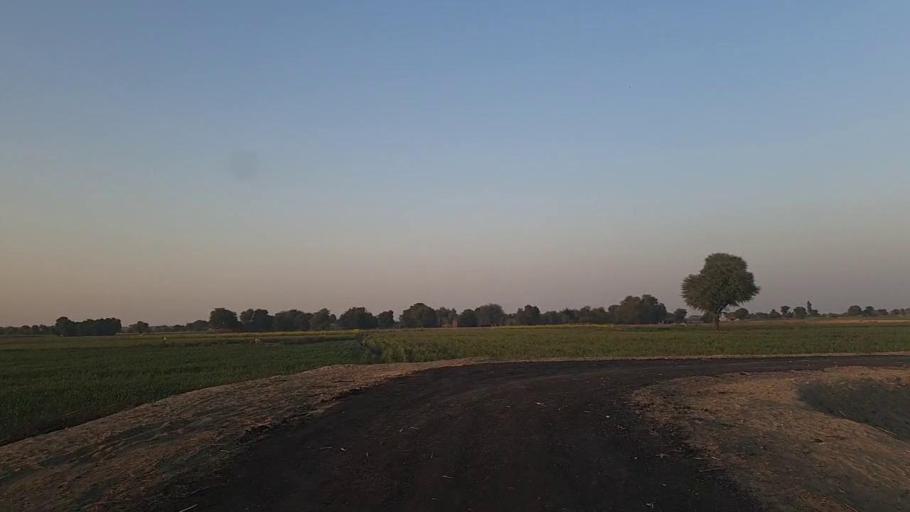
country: PK
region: Sindh
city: Jam Sahib
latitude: 26.3636
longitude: 68.7204
